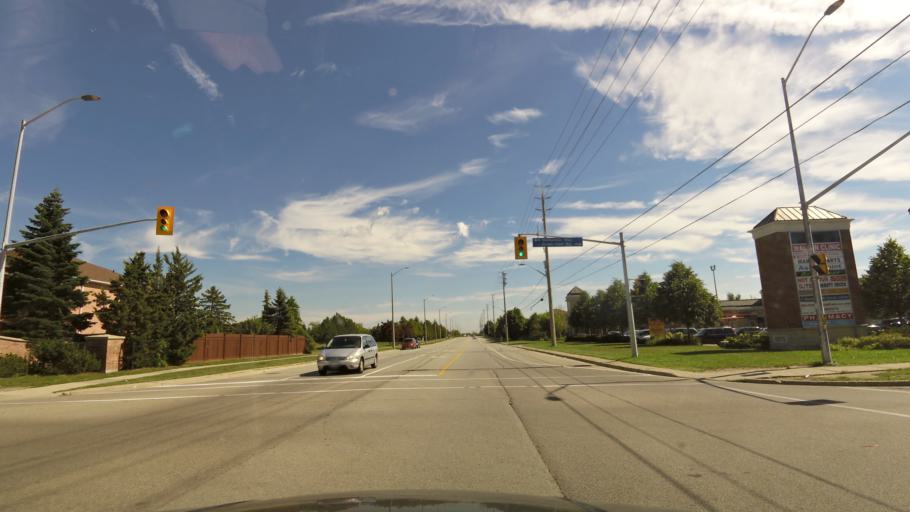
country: CA
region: Ontario
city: Mississauga
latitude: 43.5916
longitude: -79.6799
